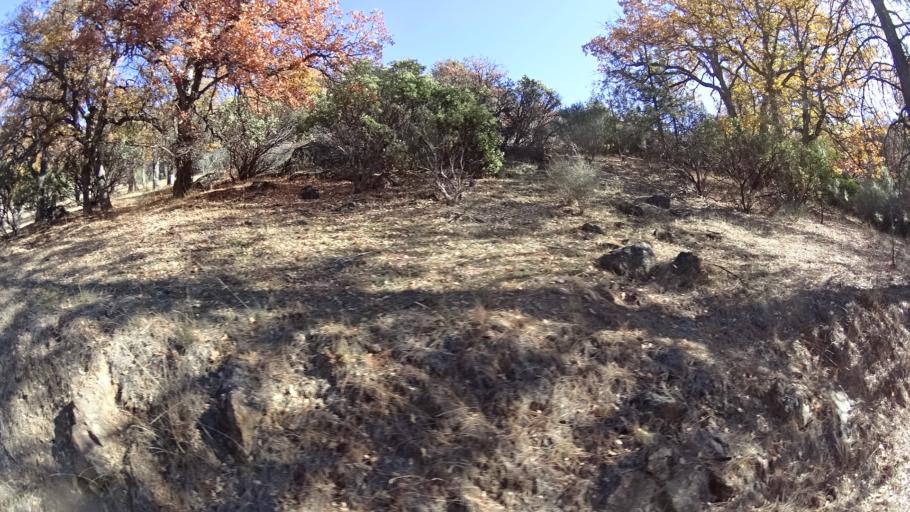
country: US
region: California
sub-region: Siskiyou County
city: Yreka
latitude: 41.8428
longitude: -122.8367
